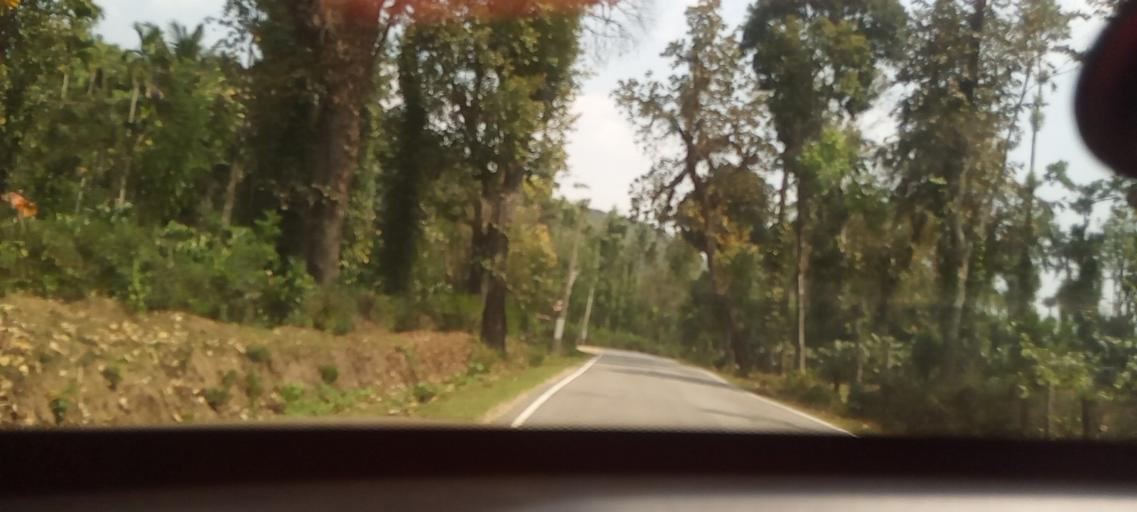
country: IN
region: Karnataka
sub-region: Chikmagalur
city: Mudigere
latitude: 13.2931
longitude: 75.5976
